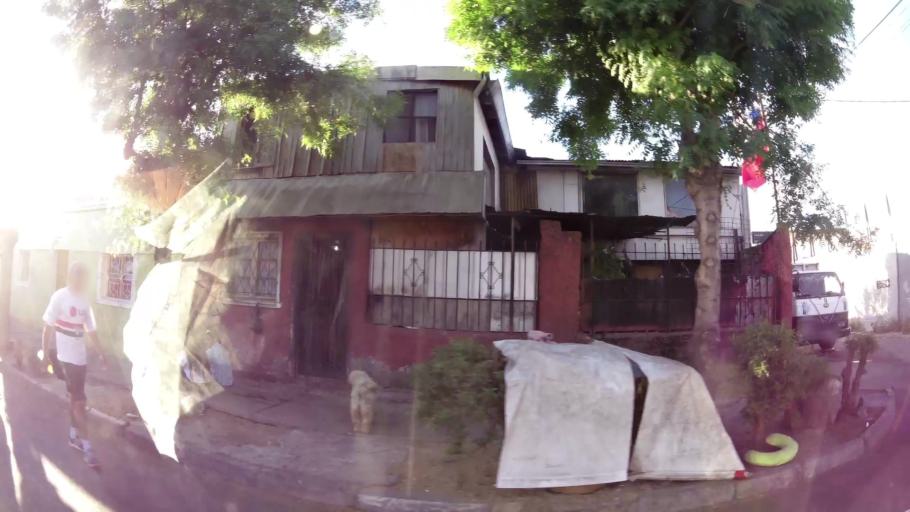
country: CL
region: Santiago Metropolitan
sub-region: Provincia de Santiago
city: Lo Prado
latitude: -33.4415
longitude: -70.7217
